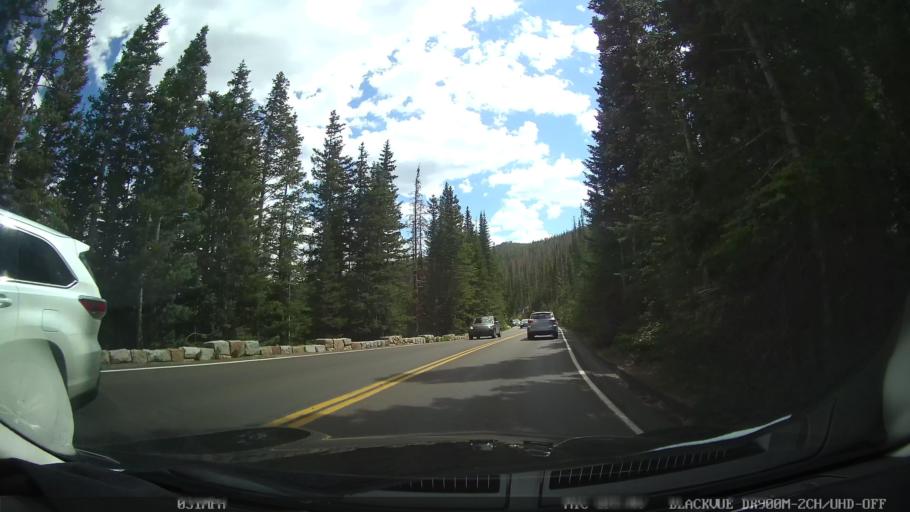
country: US
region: Colorado
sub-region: Larimer County
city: Estes Park
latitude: 40.3856
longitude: -105.6656
